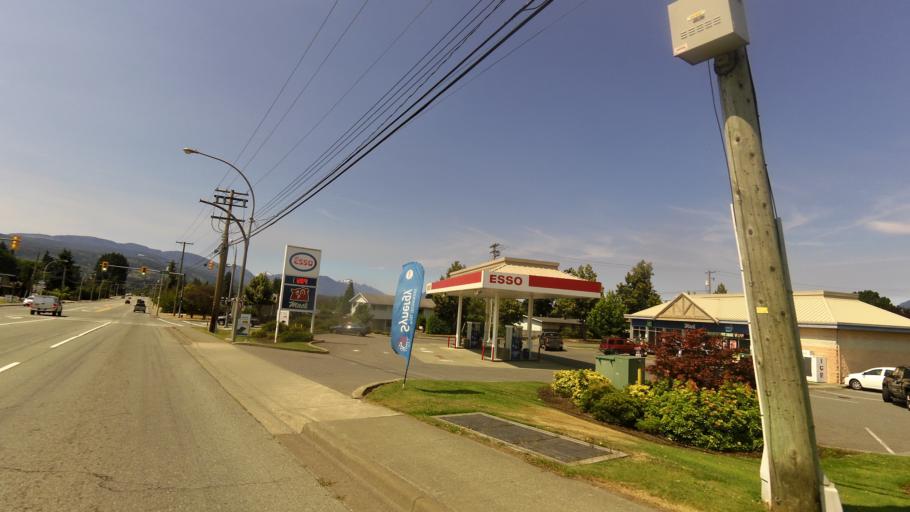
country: CA
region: British Columbia
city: Port Alberni
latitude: 49.2646
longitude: -124.7933
